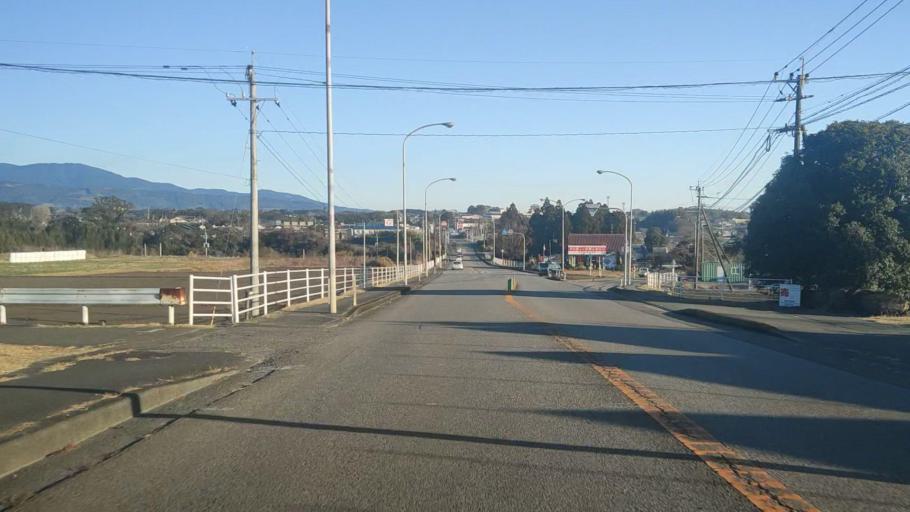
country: JP
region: Miyazaki
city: Takanabe
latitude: 32.1832
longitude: 131.5224
